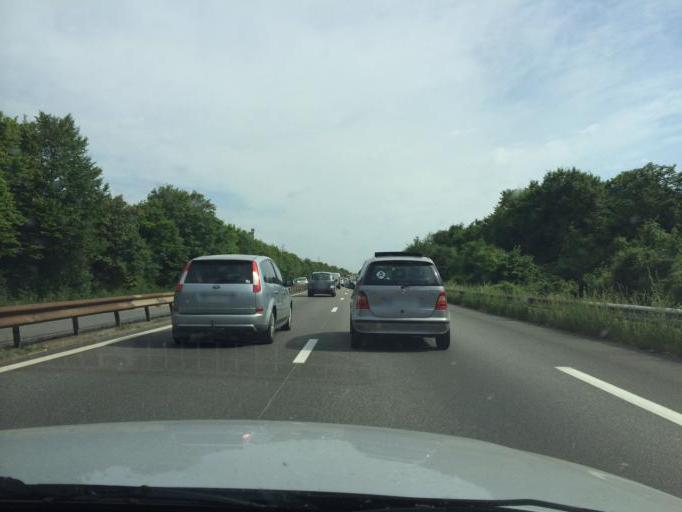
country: FR
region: Lorraine
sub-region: Departement de Meurthe-et-Moselle
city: Laxou
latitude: 48.6803
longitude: 6.1191
